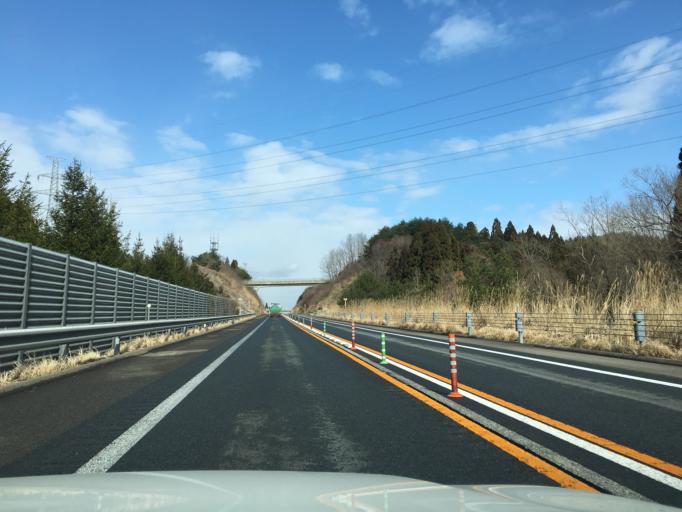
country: JP
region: Akita
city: Akita Shi
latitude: 39.8067
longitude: 140.0950
